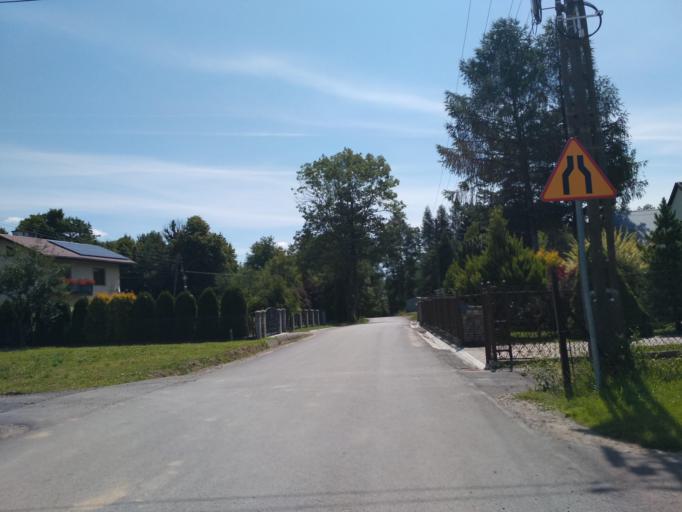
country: PL
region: Subcarpathian Voivodeship
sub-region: Powiat brzozowski
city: Jablonica Polska
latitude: 49.6925
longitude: 21.8746
